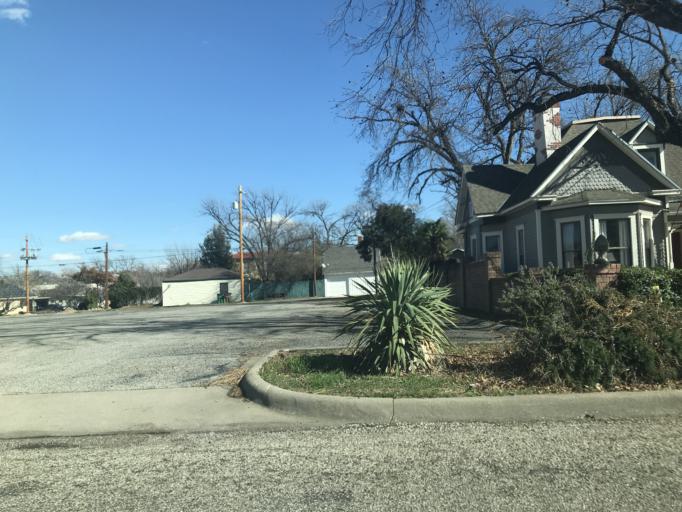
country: US
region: Texas
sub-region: Tom Green County
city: San Angelo
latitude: 31.4522
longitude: -100.4447
